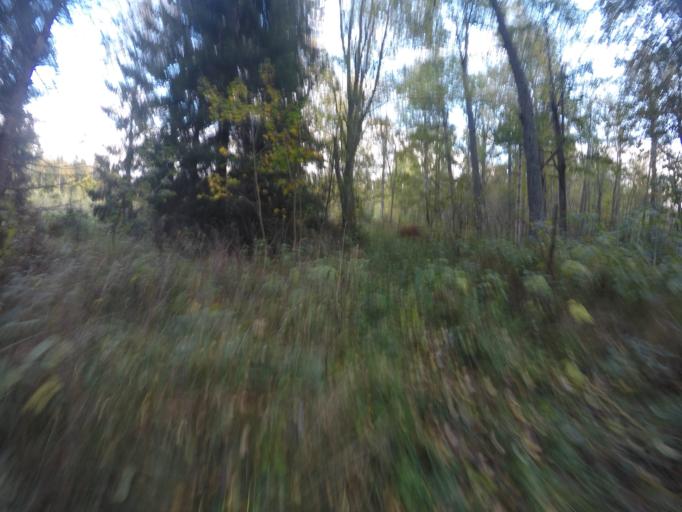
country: SE
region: Vaestmanland
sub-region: Arboga Kommun
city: Tyringe
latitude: 59.3326
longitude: 15.9676
